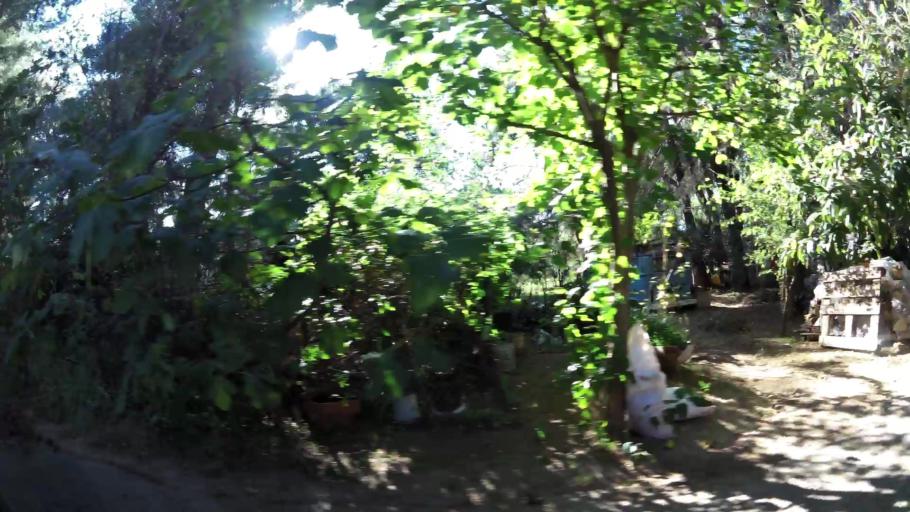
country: GR
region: Attica
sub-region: Nomarchia Athinas
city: Ekali
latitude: 38.1228
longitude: 23.8404
